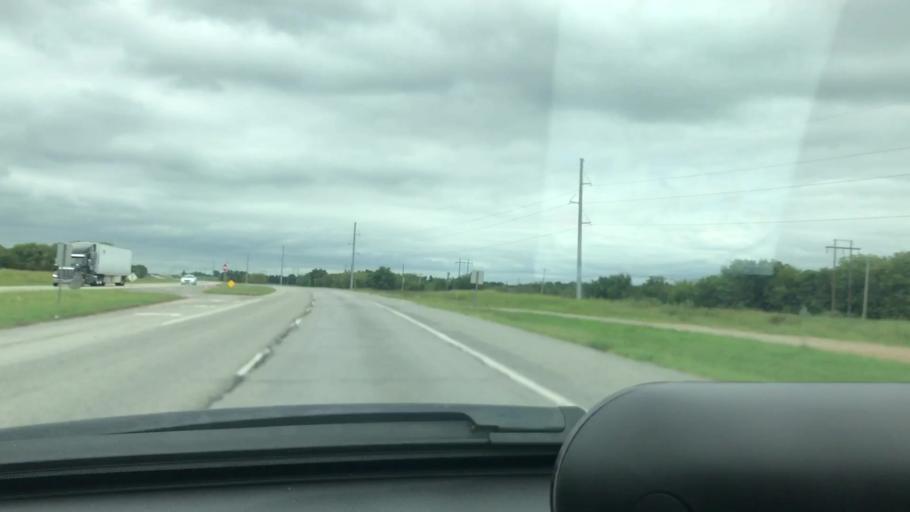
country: US
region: Oklahoma
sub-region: Wagoner County
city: Wagoner
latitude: 35.9969
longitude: -95.3690
